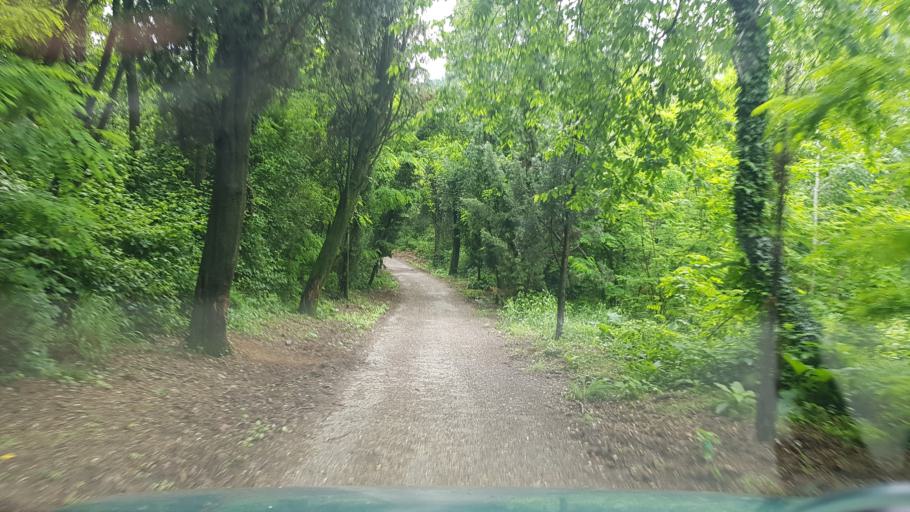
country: IT
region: Friuli Venezia Giulia
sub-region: Provincia di Gorizia
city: Gorizia
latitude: 45.9441
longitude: 13.5902
